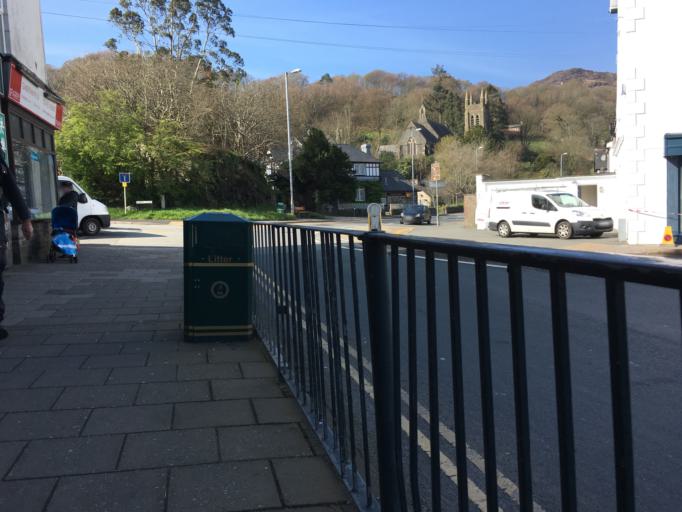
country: GB
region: Wales
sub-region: Gwynedd
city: Porthmadog
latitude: 52.9278
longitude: -4.1333
